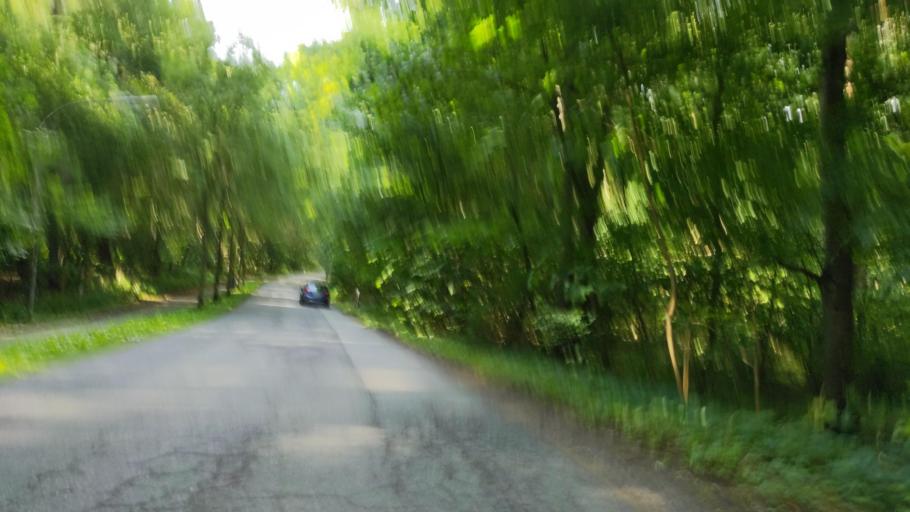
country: DE
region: Schleswig-Holstein
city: Ratekau
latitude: 53.9781
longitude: 10.7036
